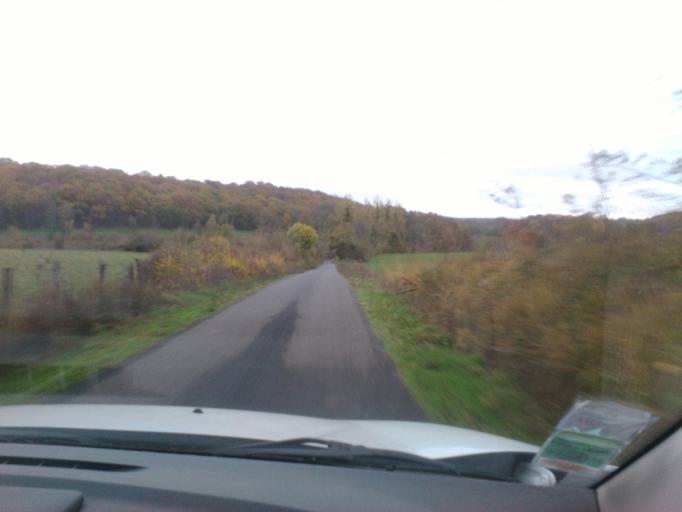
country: FR
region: Lorraine
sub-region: Departement des Vosges
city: Mirecourt
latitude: 48.2786
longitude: 6.2128
